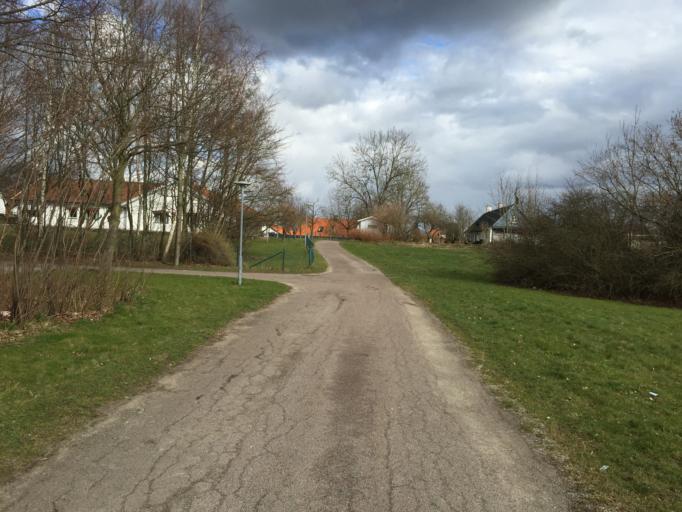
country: SE
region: Skane
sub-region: Lunds Kommun
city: Veberod
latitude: 55.6337
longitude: 13.4868
